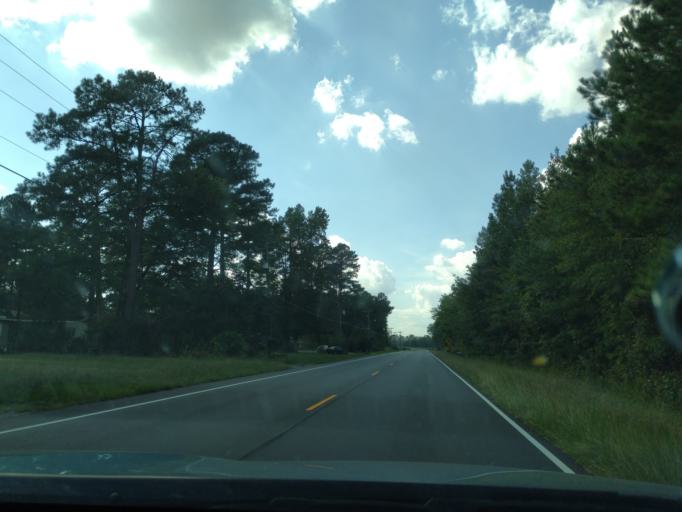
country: US
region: North Carolina
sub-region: Pitt County
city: Bethel
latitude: 35.8247
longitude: -77.3217
